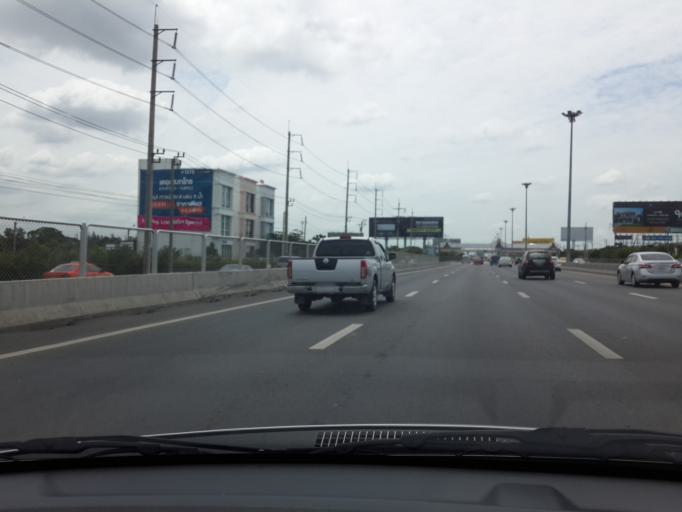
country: TH
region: Bangkok
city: Suan Luang
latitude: 13.7369
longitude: 100.6677
